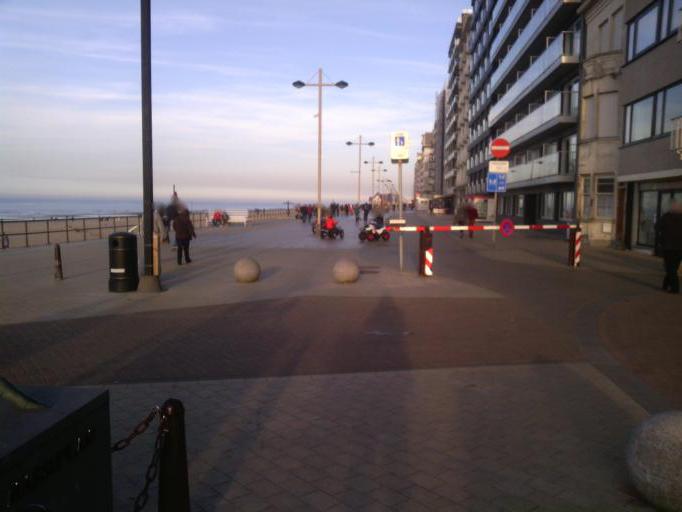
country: BE
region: Flanders
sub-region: Provincie West-Vlaanderen
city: Middelkerke
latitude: 51.1821
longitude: 2.8007
